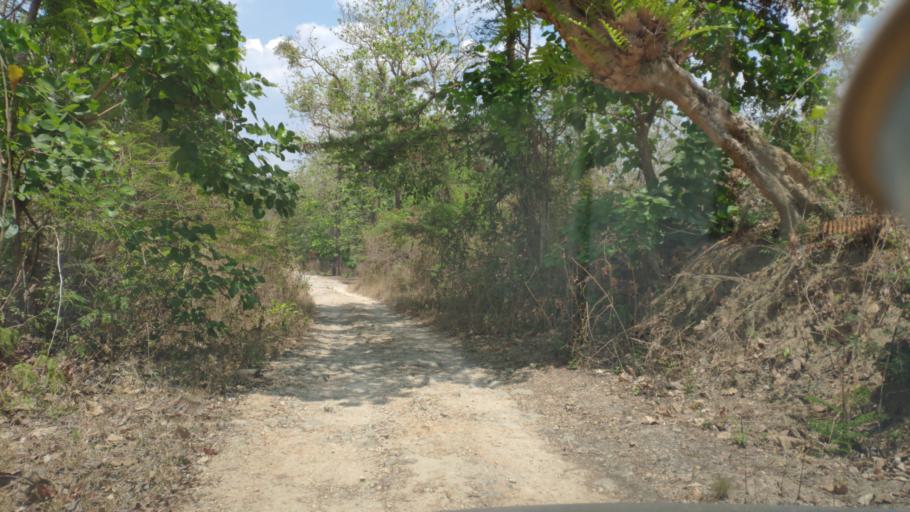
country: ID
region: Central Java
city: Suruhan
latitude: -6.9966
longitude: 111.5247
